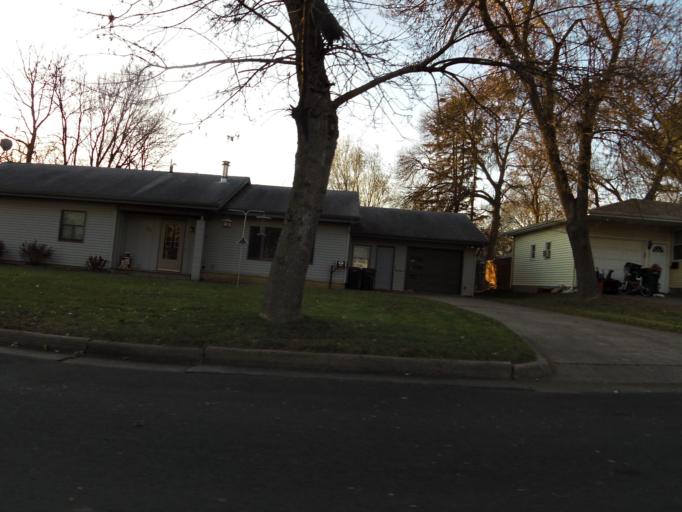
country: US
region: Wisconsin
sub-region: Pierce County
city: River Falls
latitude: 44.8635
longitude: -92.6166
